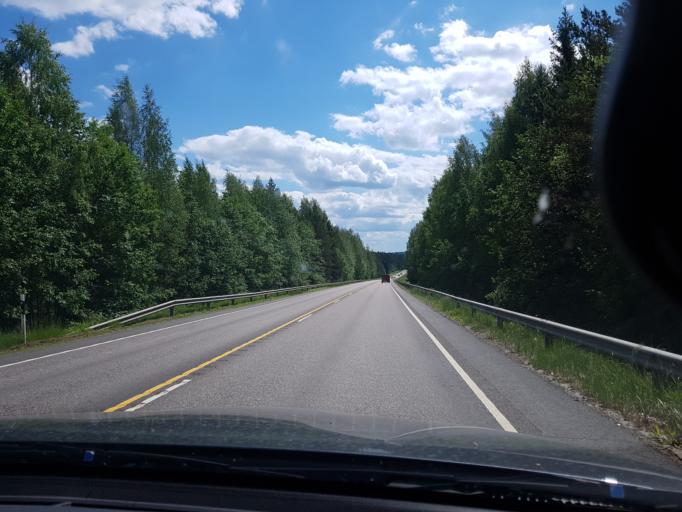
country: FI
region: Haeme
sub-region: Haemeenlinna
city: Parola
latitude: 61.1294
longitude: 24.4182
